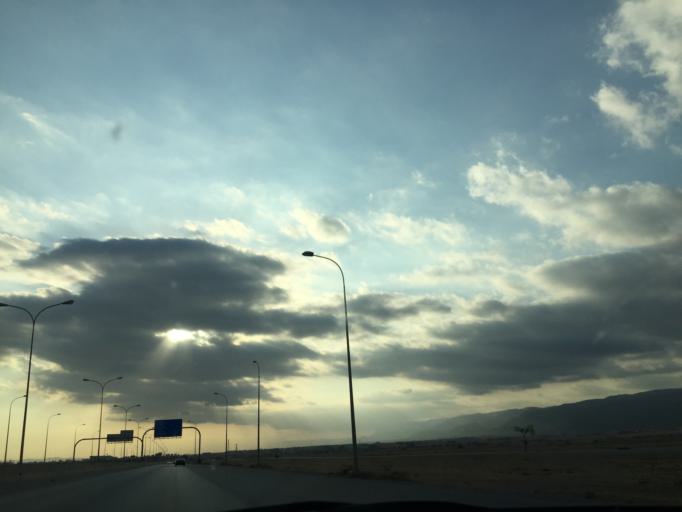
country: OM
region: Zufar
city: Salalah
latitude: 17.0559
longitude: 54.0765
